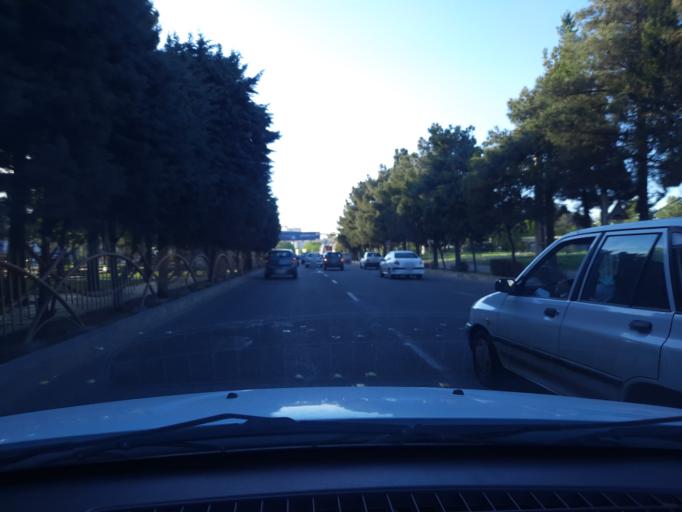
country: IR
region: Qazvin
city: Qazvin
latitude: 36.2816
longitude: 50.0225
